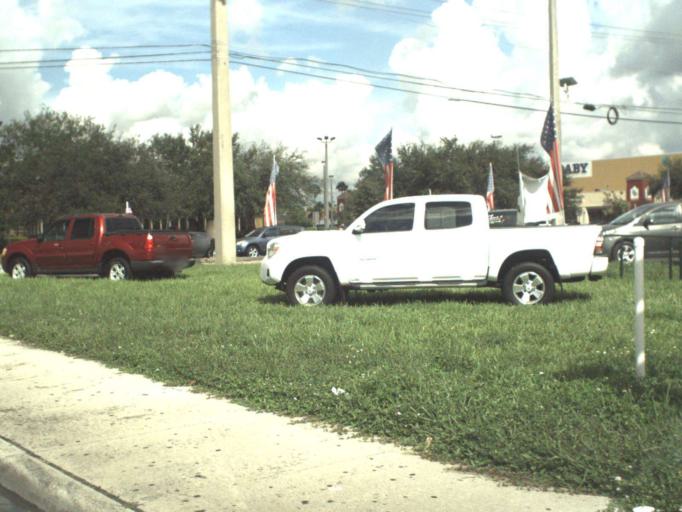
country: US
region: Florida
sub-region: Miami-Dade County
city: Flagami
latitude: 25.7699
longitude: -80.3278
